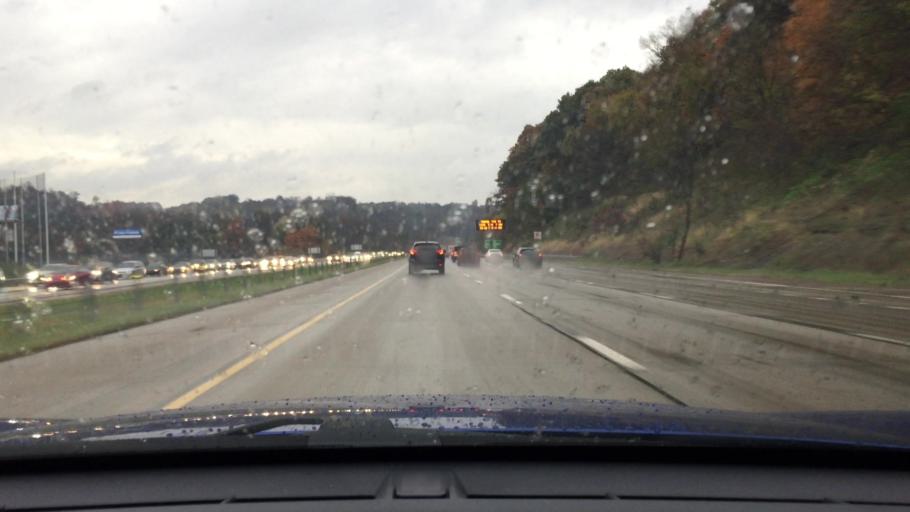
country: US
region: Pennsylvania
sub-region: Allegheny County
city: Bridgeville
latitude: 40.3641
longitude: -80.1188
